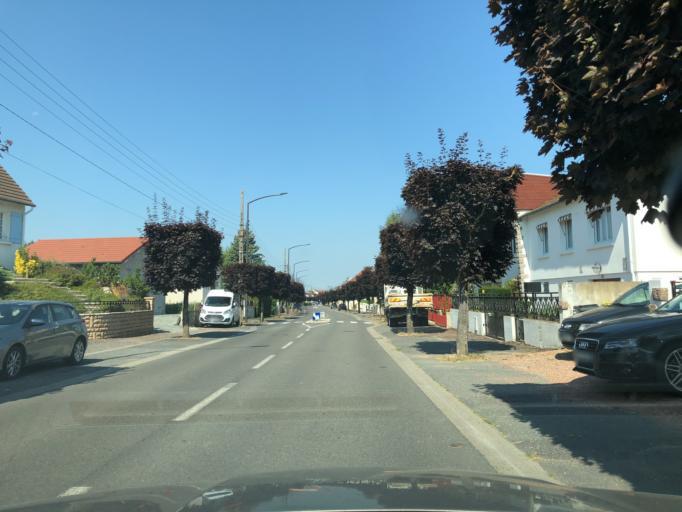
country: FR
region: Auvergne
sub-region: Departement de l'Allier
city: Cusset
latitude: 46.1329
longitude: 3.4696
